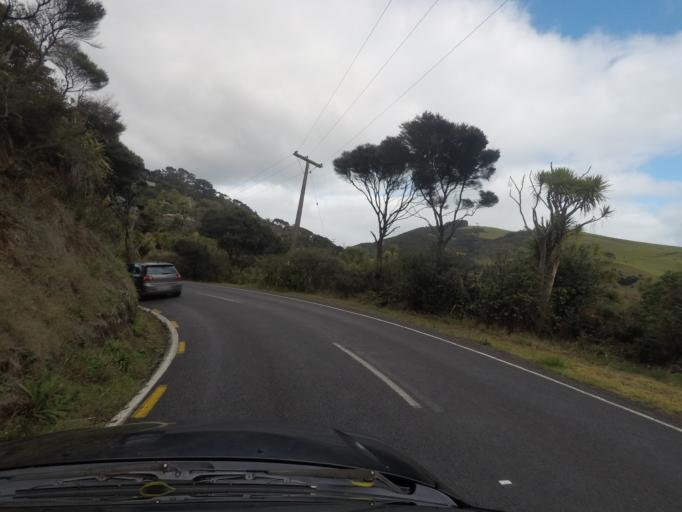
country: NZ
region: Auckland
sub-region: Auckland
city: Muriwai Beach
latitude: -36.8784
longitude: 174.4522
